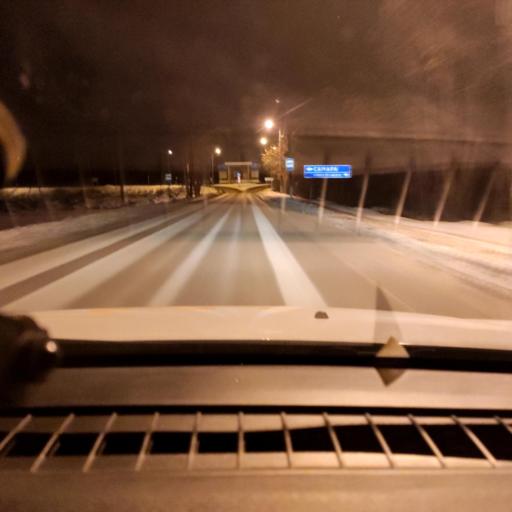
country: RU
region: Samara
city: Novokuybyshevsk
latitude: 53.1439
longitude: 49.9846
